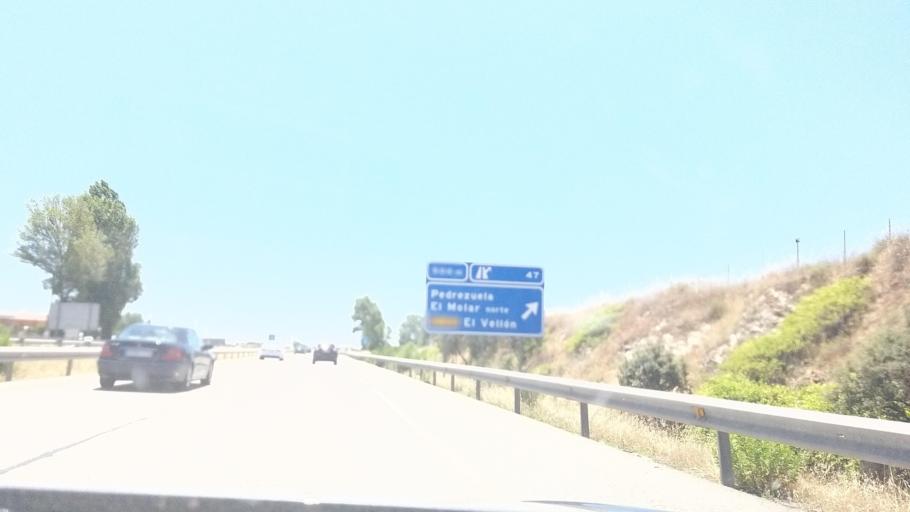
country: ES
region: Madrid
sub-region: Provincia de Madrid
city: Venturada
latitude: 40.7735
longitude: -3.6087
